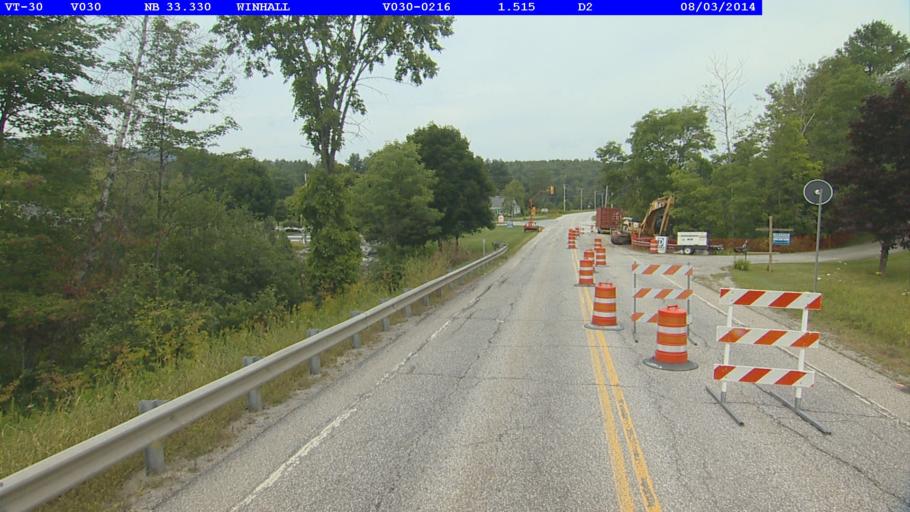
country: US
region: Vermont
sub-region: Bennington County
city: Manchester Center
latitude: 43.1464
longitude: -72.8952
